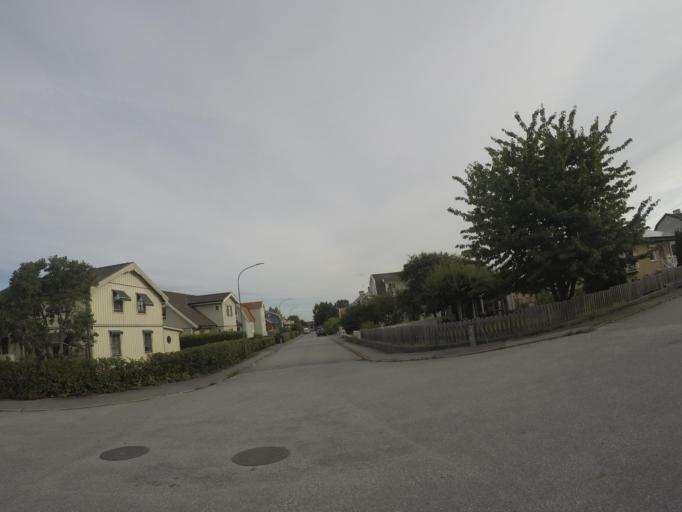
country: SE
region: OErebro
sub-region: Orebro Kommun
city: Orebro
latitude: 59.2624
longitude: 15.2444
